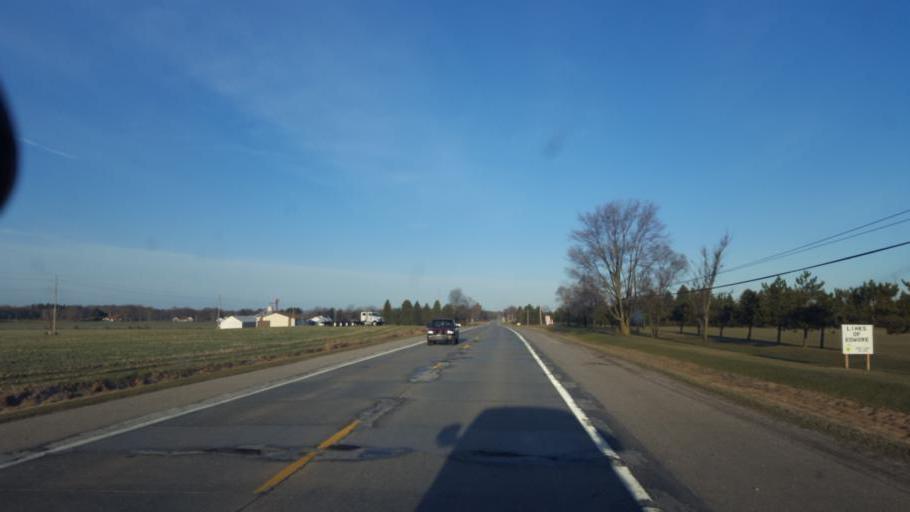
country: US
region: Michigan
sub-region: Montcalm County
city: Edmore
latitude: 43.4083
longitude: -85.0544
